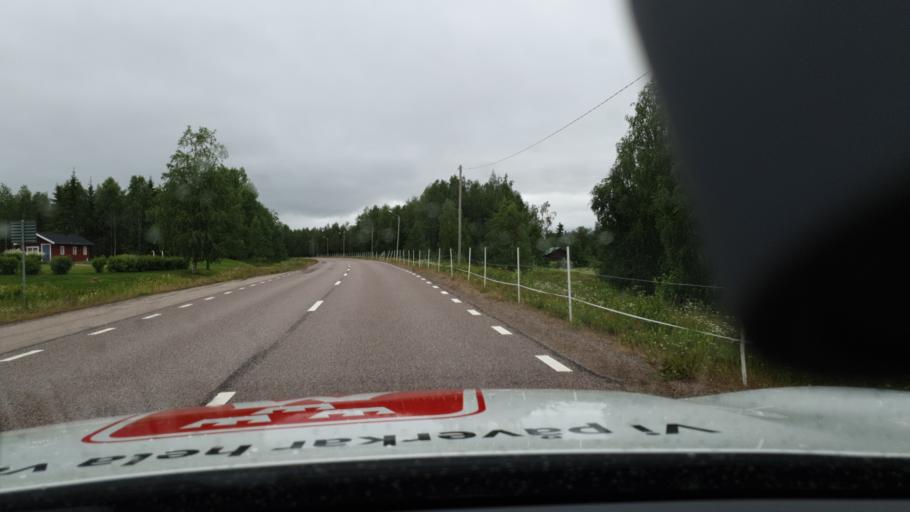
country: FI
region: Lapland
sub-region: Torniolaakso
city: Pello
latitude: 66.9558
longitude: 23.8407
